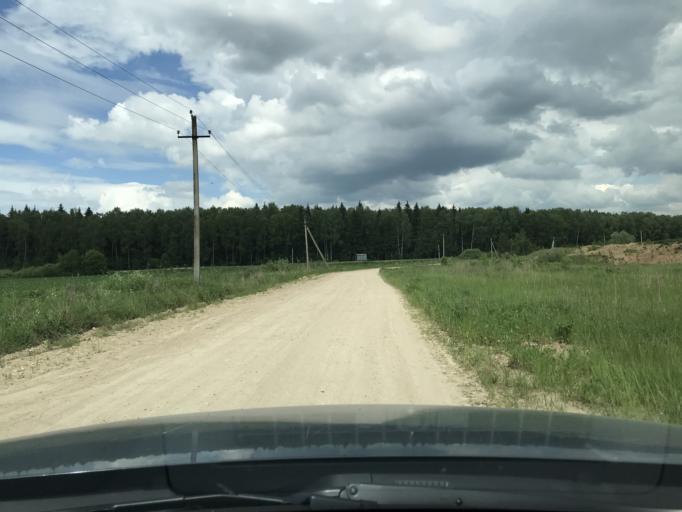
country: RU
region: Moskovskaya
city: Vereya
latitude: 55.3215
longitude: 36.3206
